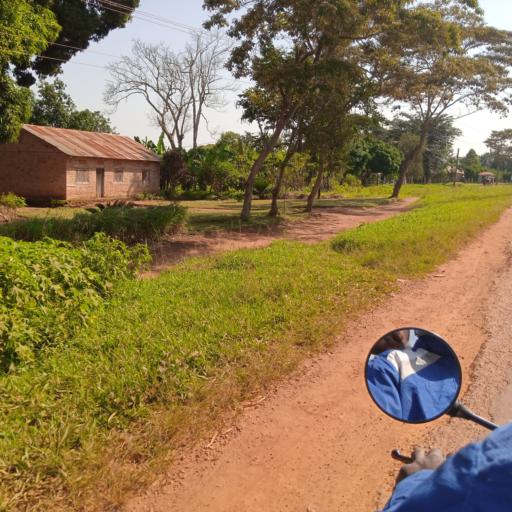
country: UG
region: Central Region
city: Masaka
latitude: -0.3808
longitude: 31.7045
